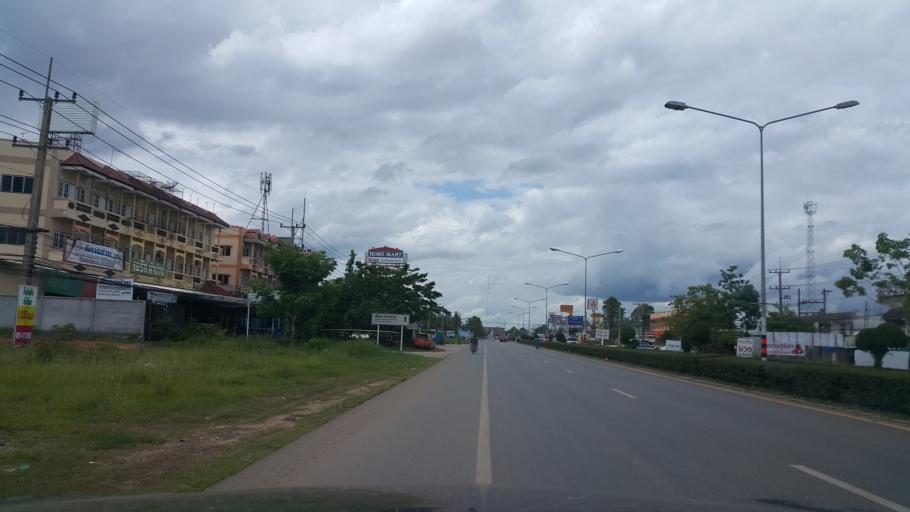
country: TH
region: Sukhothai
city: Sukhothai
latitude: 17.0154
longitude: 99.8095
